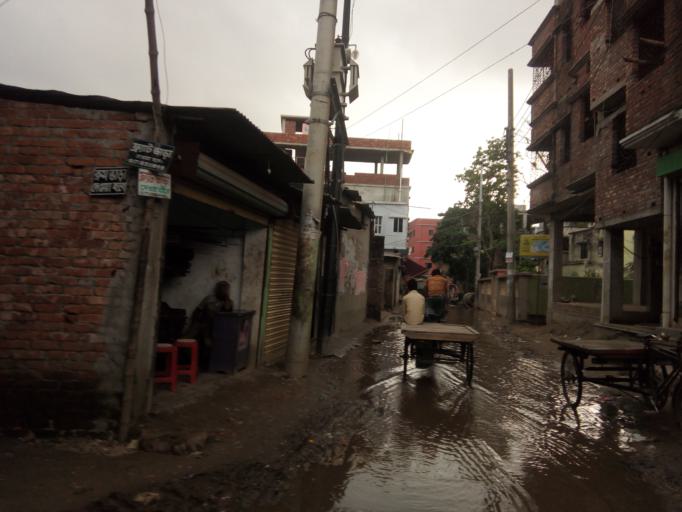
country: BD
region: Dhaka
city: Azimpur
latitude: 23.7191
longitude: 90.3634
